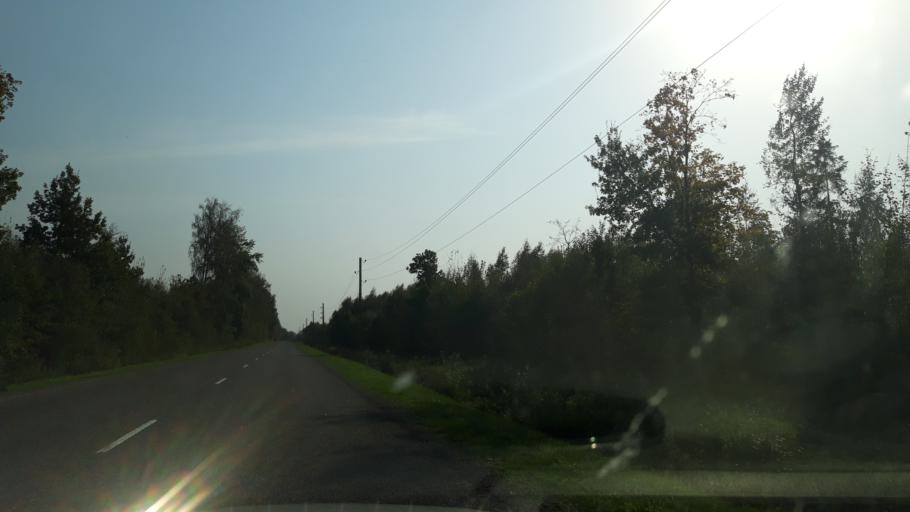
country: LV
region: Burtnieki
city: Matisi
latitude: 57.6350
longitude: 25.2571
